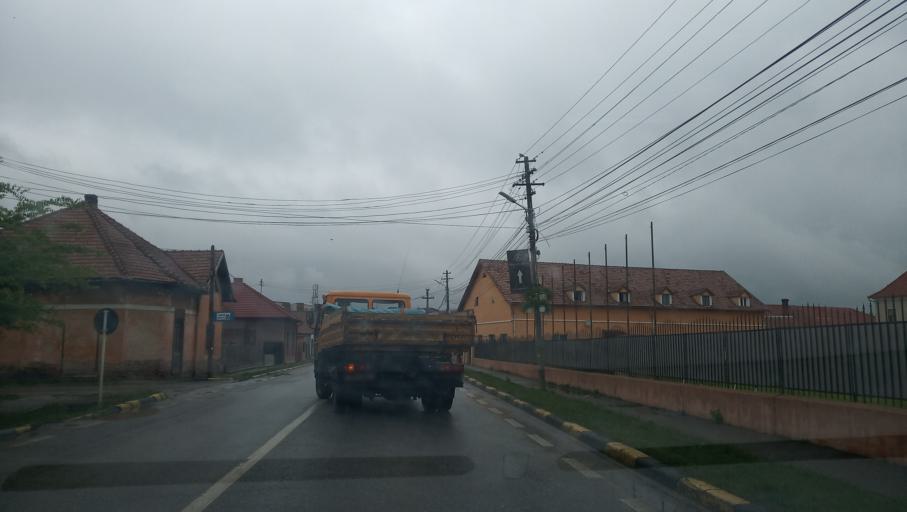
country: RO
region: Alba
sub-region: Municipiul Sebes
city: Sebes
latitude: 45.9535
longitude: 23.5799
